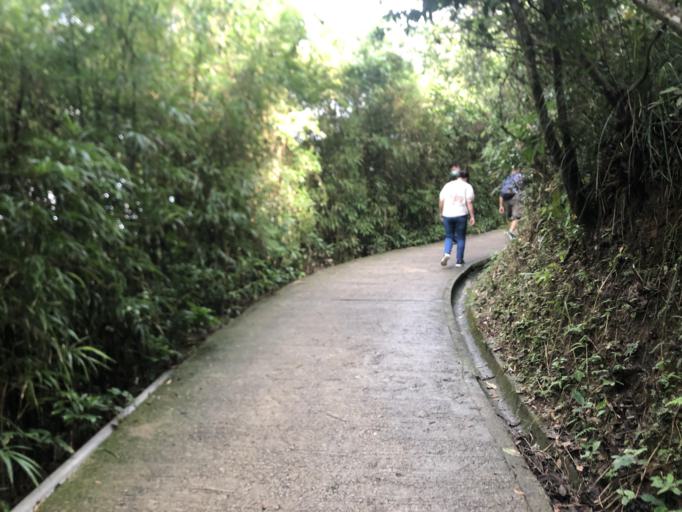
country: HK
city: Hong Kong
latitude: 22.2785
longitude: 114.1364
